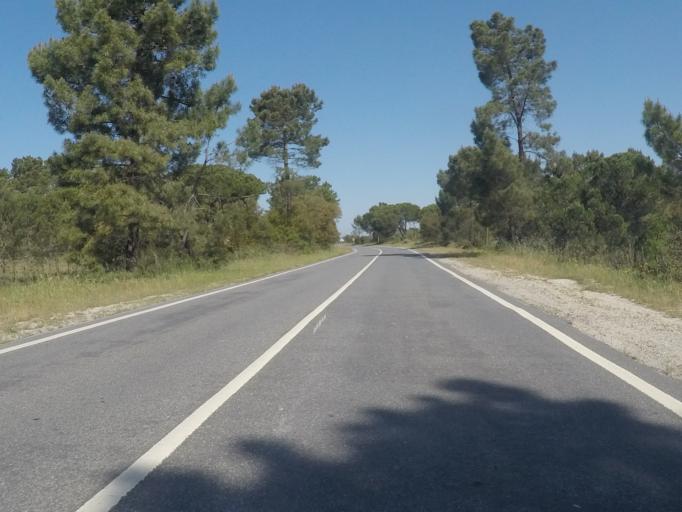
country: PT
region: Setubal
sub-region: Grandola
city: Grandola
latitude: 38.2978
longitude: -8.7252
